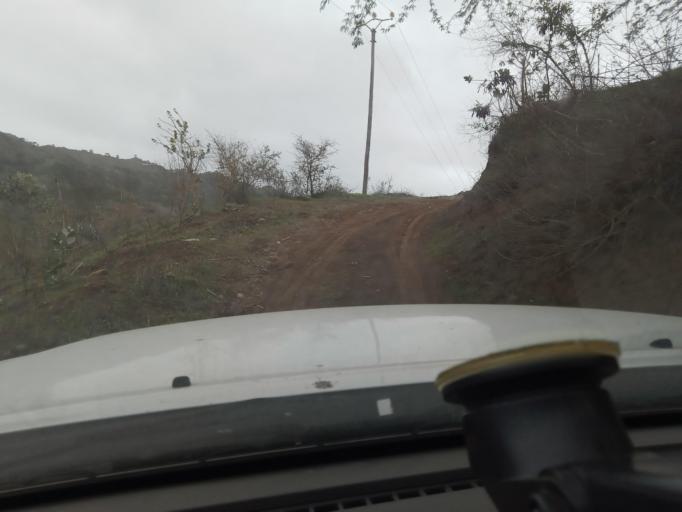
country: CV
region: Sao Salvador do Mundo
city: Picos
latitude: 15.1410
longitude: -23.6348
